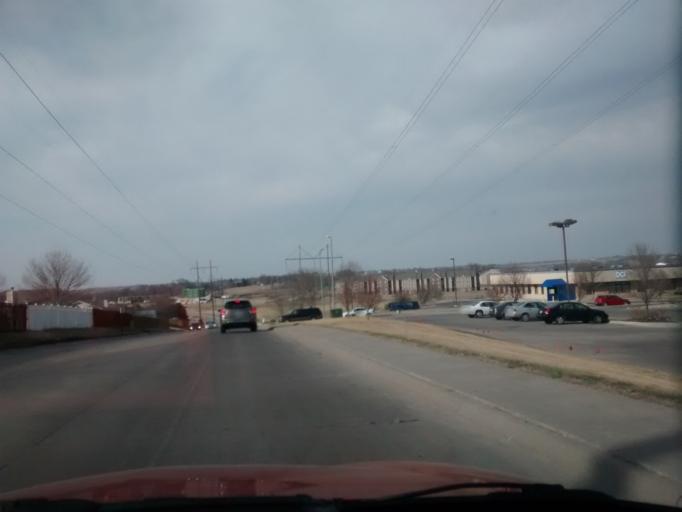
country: US
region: Nebraska
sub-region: Sarpy County
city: Offutt Air Force Base
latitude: 41.1409
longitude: -95.9762
